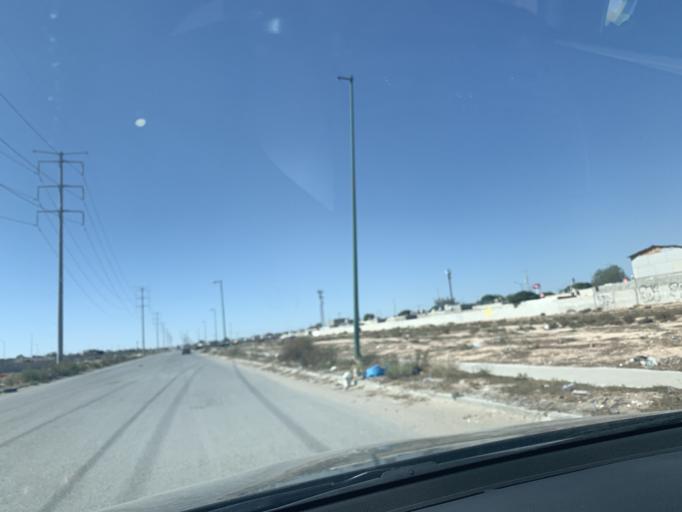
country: US
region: Texas
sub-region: El Paso County
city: Socorro Mission Number 1 Colonia
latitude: 31.5934
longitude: -106.3455
